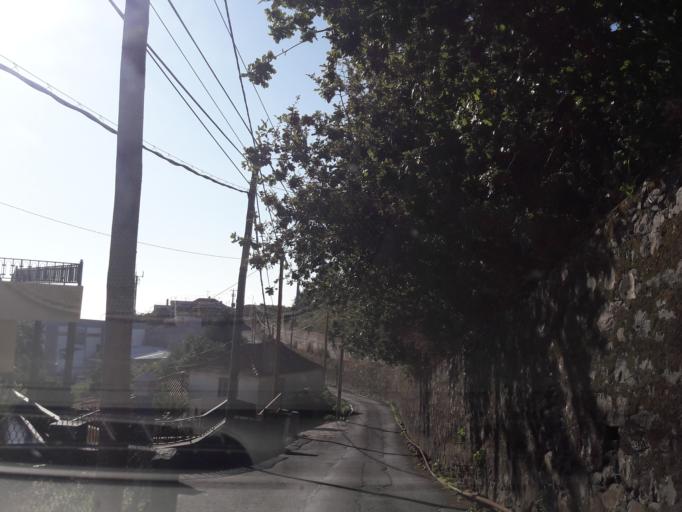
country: PT
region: Madeira
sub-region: Santa Cruz
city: Camacha
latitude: 32.6620
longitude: -16.8642
